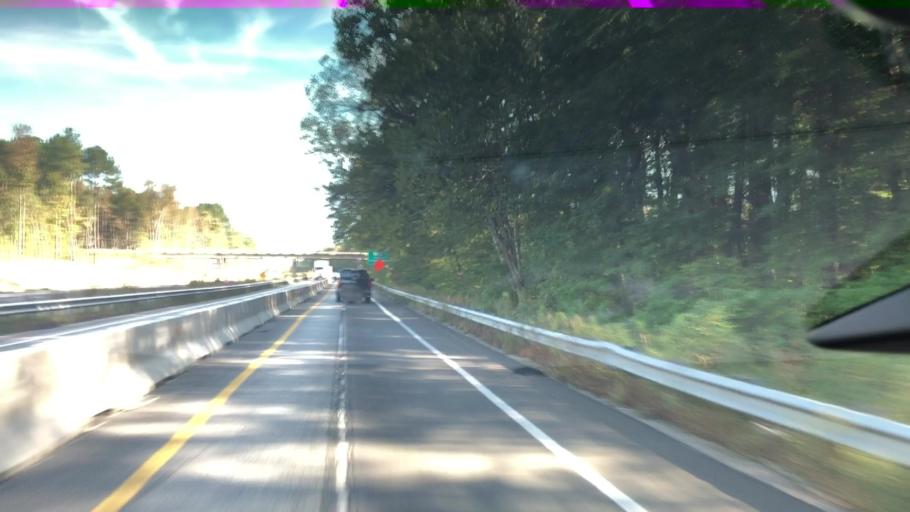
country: US
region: North Carolina
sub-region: Vance County
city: Henderson
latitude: 36.3809
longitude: -78.3498
